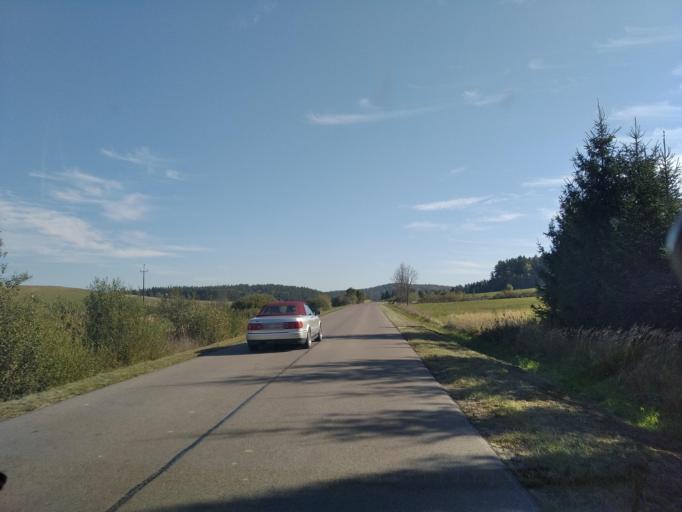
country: PL
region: Subcarpathian Voivodeship
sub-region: Powiat sanocki
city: Bukowsko
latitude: 49.4138
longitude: 21.9429
